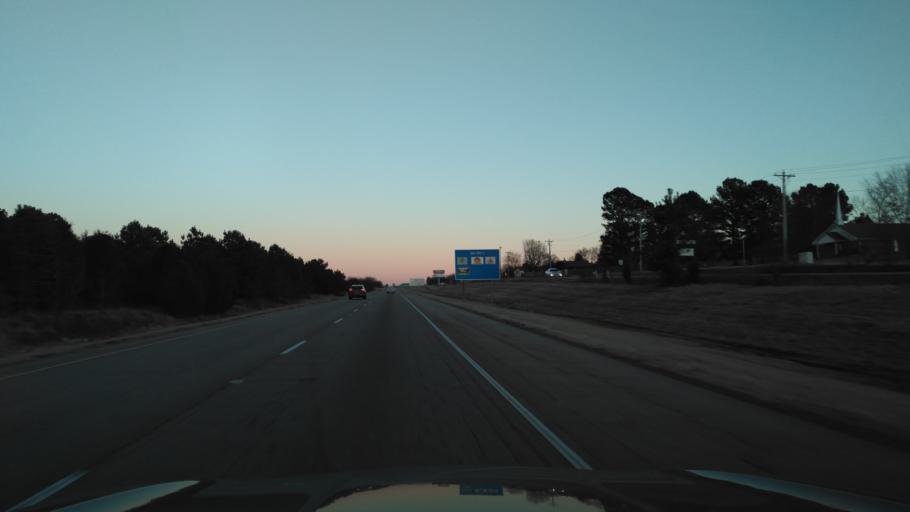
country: US
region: Arkansas
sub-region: Crawford County
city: Van Buren
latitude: 35.4648
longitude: -94.3731
